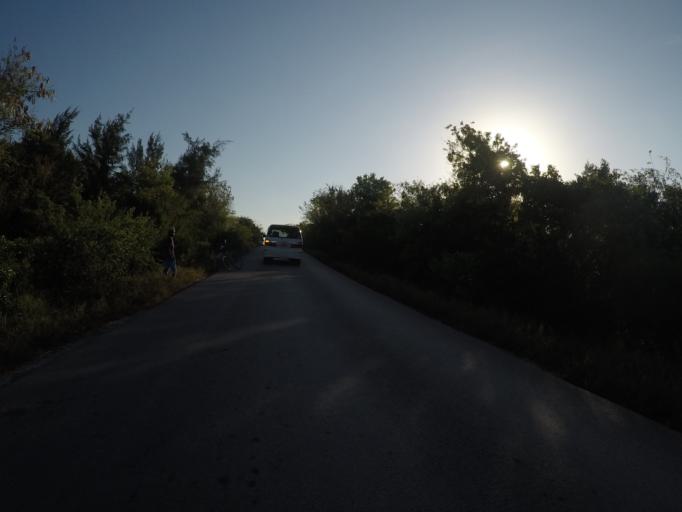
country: TZ
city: Kiwengwa
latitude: -6.1419
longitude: 39.5107
